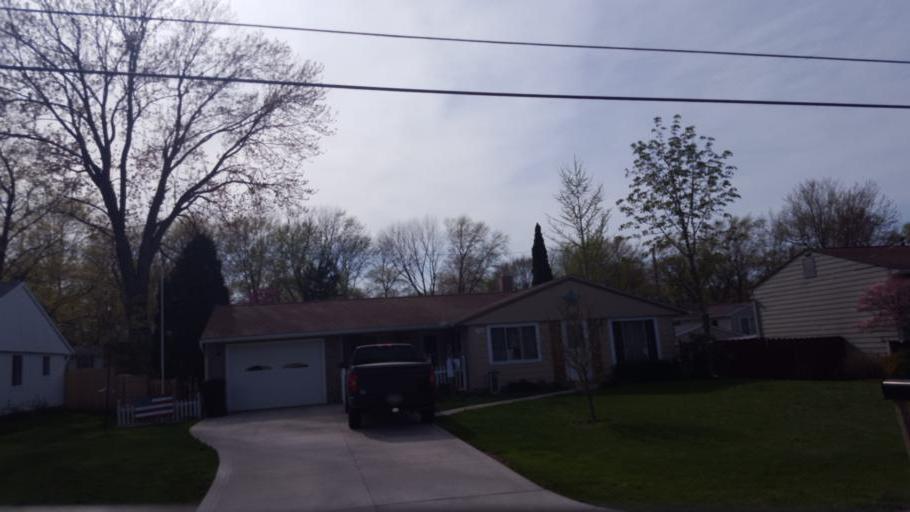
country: US
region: Ohio
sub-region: Lake County
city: North Madison
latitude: 41.8281
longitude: -81.0618
